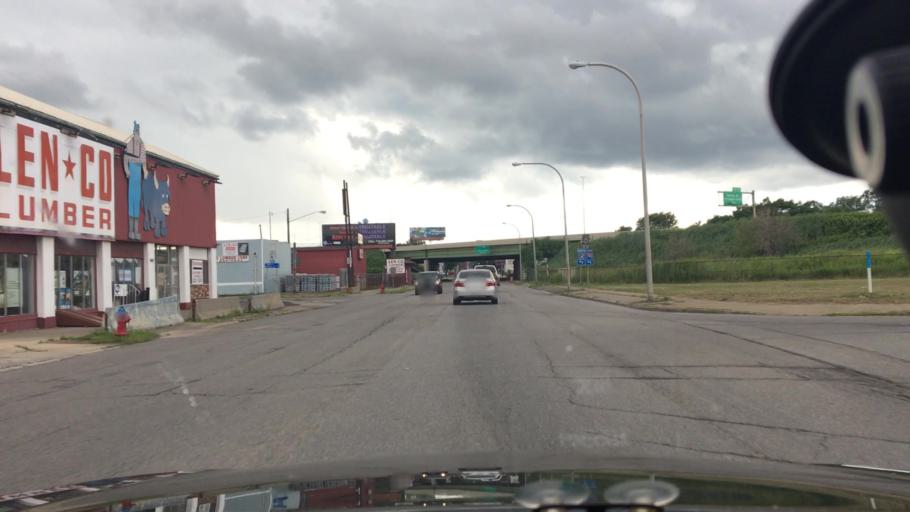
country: US
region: New York
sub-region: Erie County
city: West Seneca
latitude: 42.8669
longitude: -78.8253
